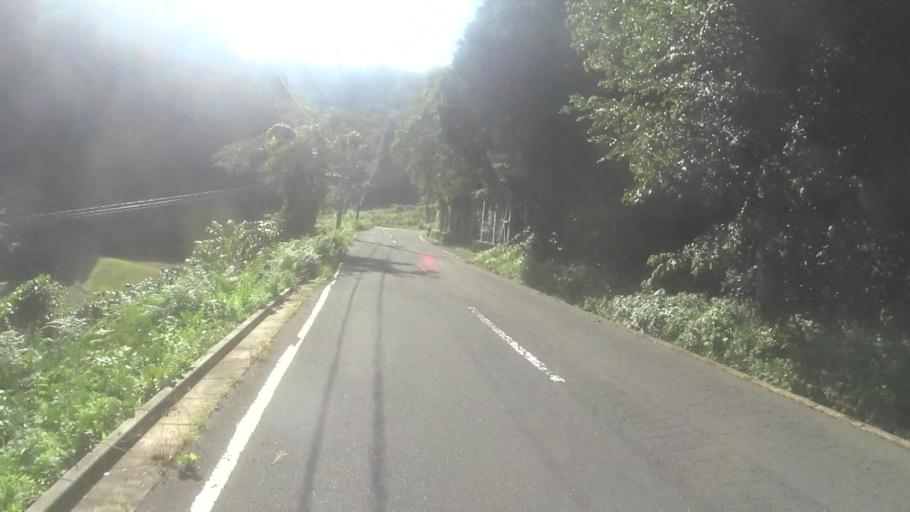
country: JP
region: Kyoto
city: Miyazu
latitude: 35.6940
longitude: 135.1436
